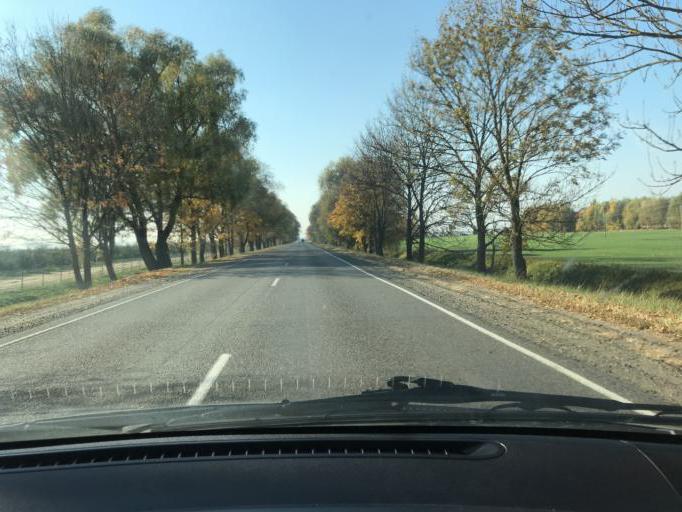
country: BY
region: Brest
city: Davyd-Haradok
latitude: 52.0594
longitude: 27.2703
